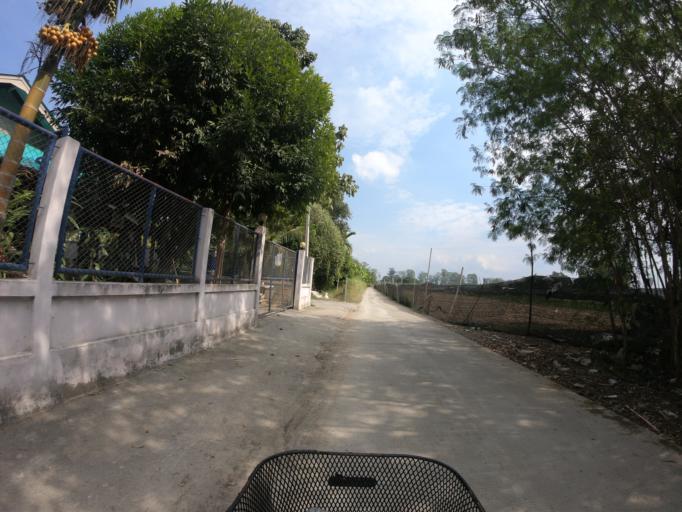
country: TH
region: Chiang Mai
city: Saraphi
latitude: 18.7046
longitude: 99.0323
